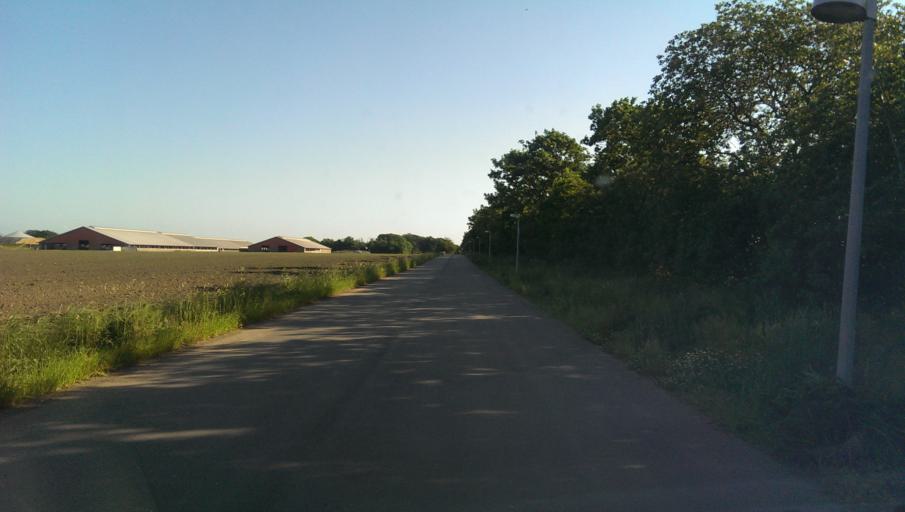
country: DK
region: South Denmark
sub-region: Esbjerg Kommune
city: Bramming
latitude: 55.5282
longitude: 8.7028
